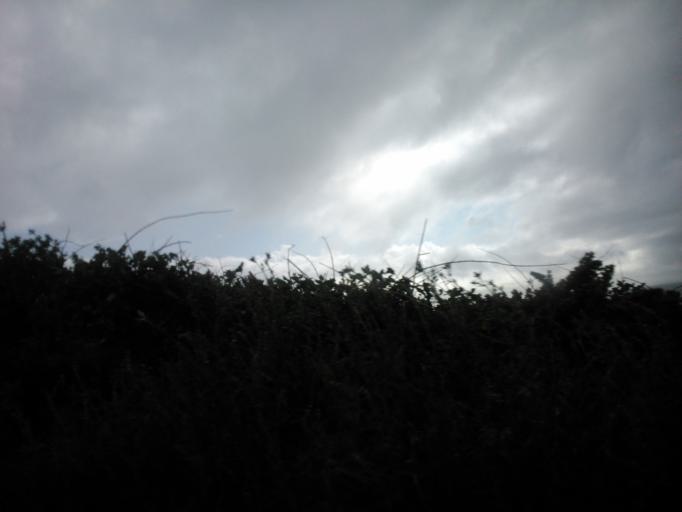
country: CL
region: Araucania
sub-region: Provincia de Cautin
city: Carahue
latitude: -38.8139
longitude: -73.3970
